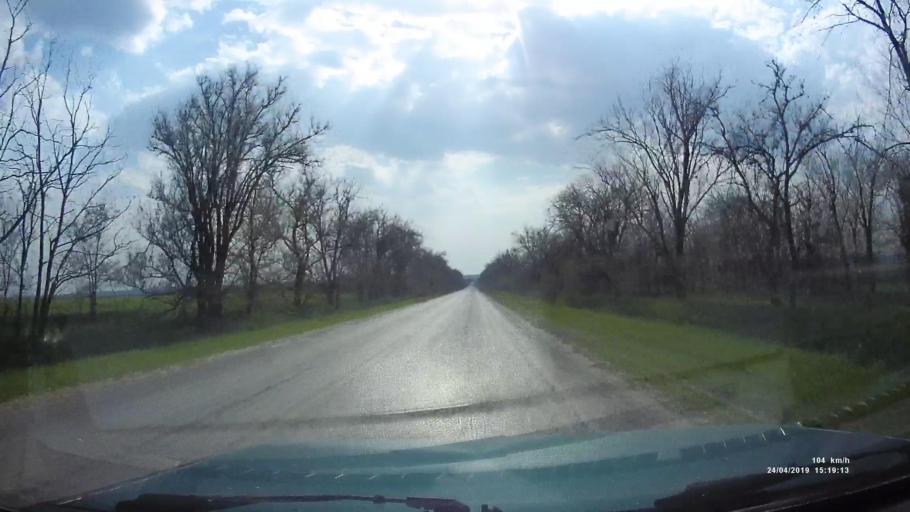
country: RU
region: Rostov
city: Remontnoye
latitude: 46.5415
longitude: 43.1506
